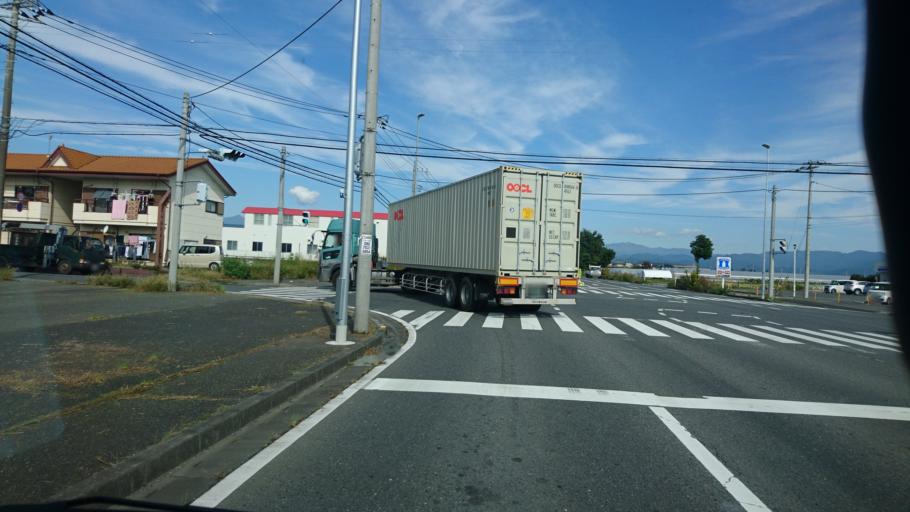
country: JP
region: Gunma
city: Kiryu
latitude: 36.3606
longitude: 139.2801
